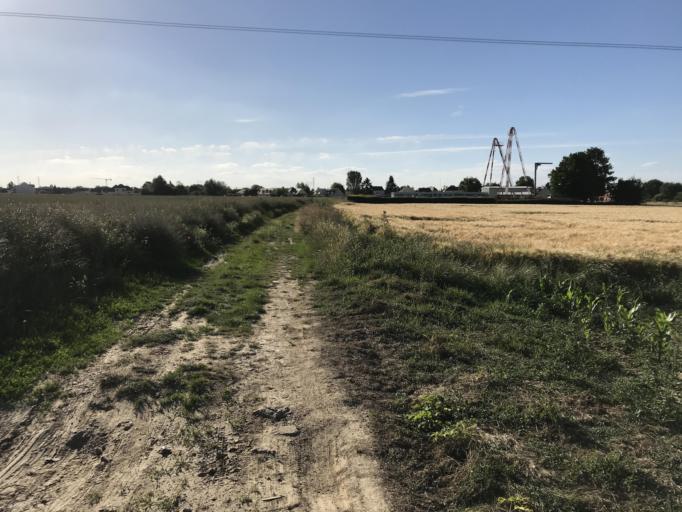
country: FR
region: Ile-de-France
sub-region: Departement de l'Essonne
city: Villejust
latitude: 48.6699
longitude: 2.2214
